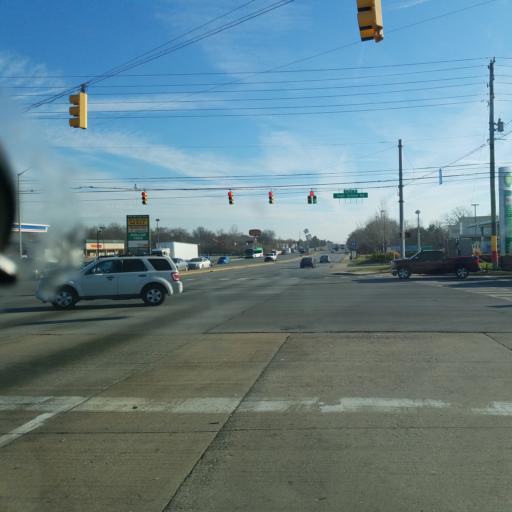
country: US
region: Indiana
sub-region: Marion County
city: Speedway
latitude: 39.8234
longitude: -86.2706
